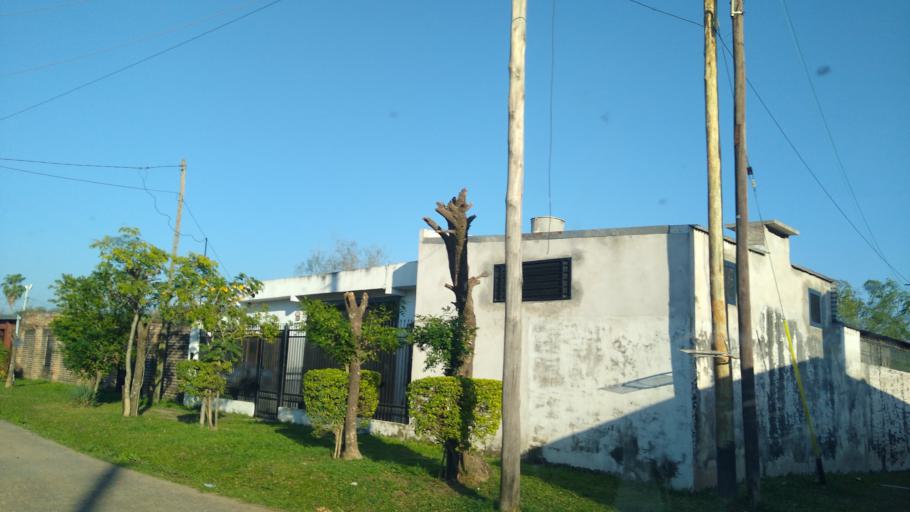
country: AR
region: Chaco
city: Barranqueras
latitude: -27.4790
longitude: -58.9482
